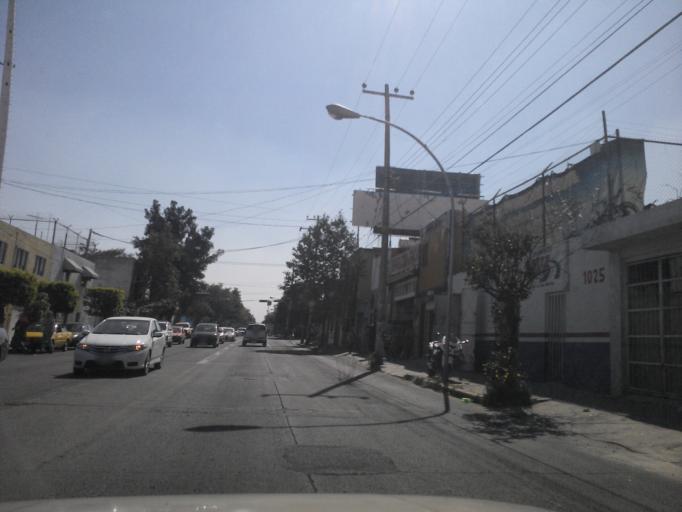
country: MX
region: Jalisco
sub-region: Zapopan
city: Zapopan
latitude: 20.6940
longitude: -103.3585
